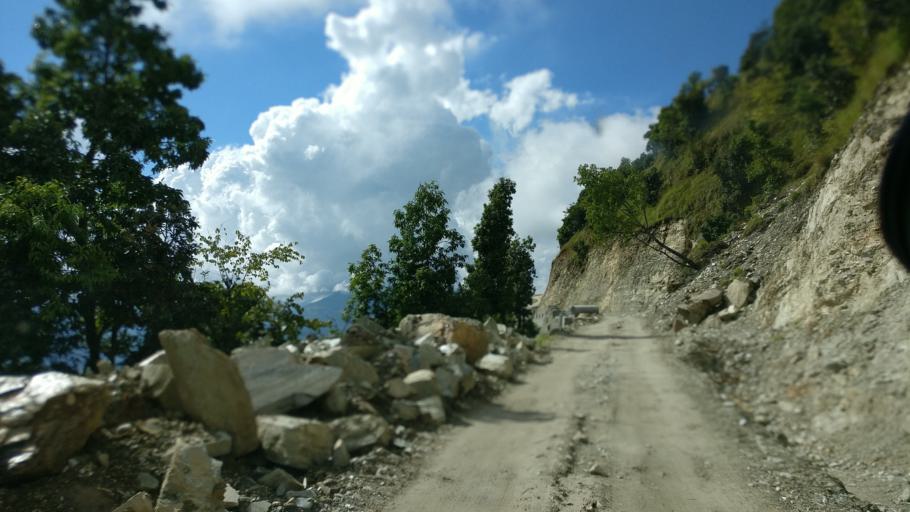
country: NP
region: Western Region
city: Baglung
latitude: 28.2811
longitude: 83.6414
